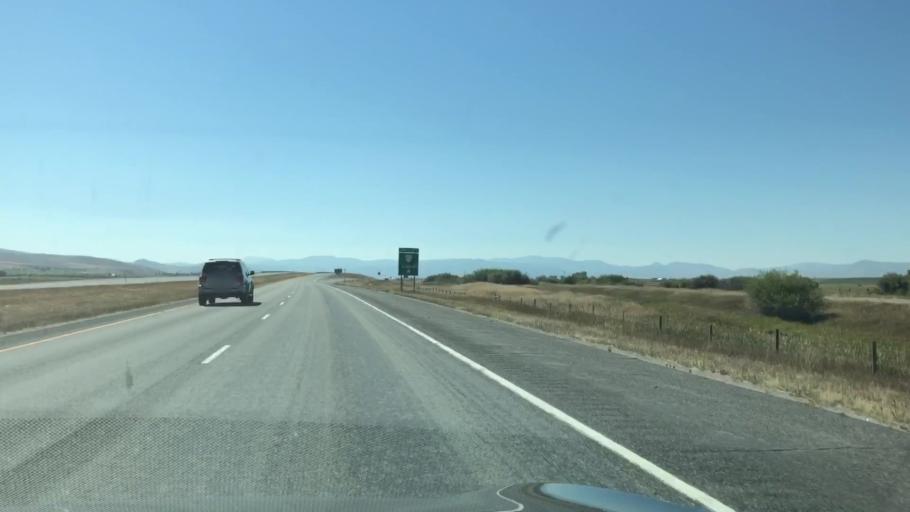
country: US
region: Montana
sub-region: Deer Lodge County
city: Warm Springs
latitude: 46.2435
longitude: -112.7640
